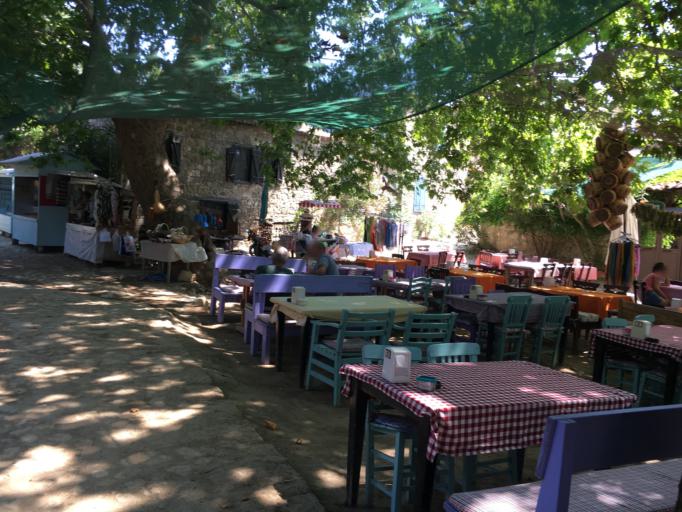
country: TR
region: Canakkale
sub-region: Merkez
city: Kucukkuyu
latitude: 39.5698
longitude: 26.6186
